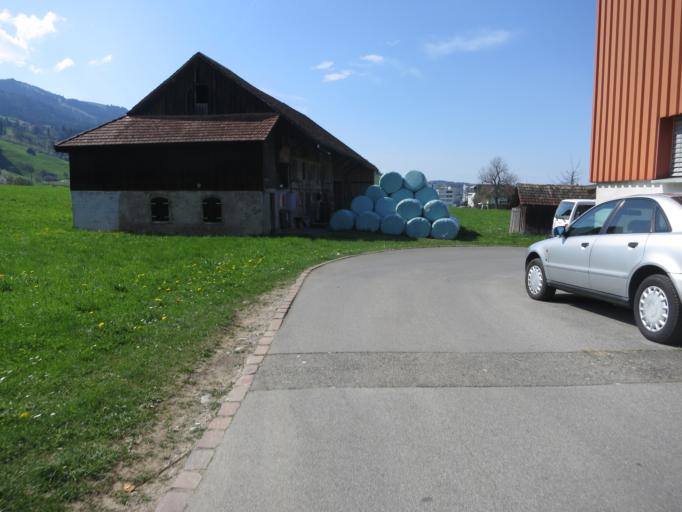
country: CH
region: Schwyz
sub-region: Bezirk March
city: Lachen
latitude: 47.1844
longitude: 8.8551
